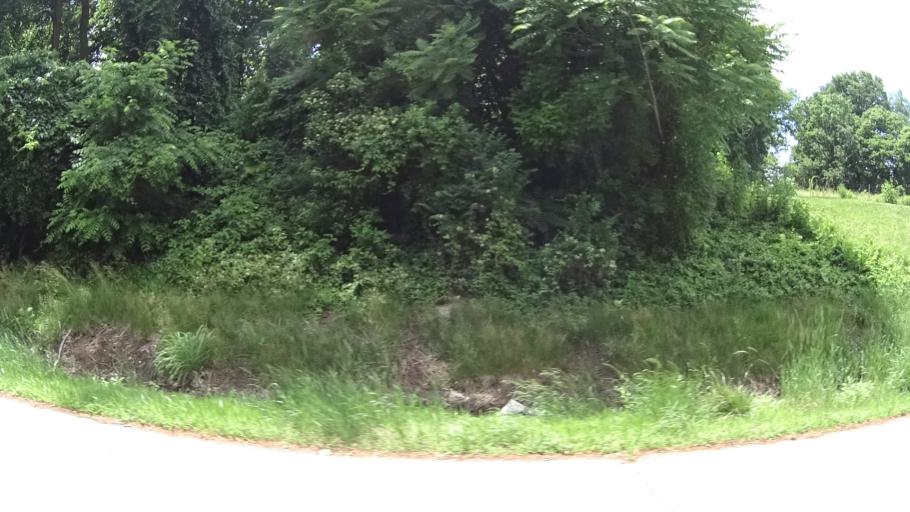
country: US
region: Ohio
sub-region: Erie County
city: Milan
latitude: 41.2872
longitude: -82.6055
